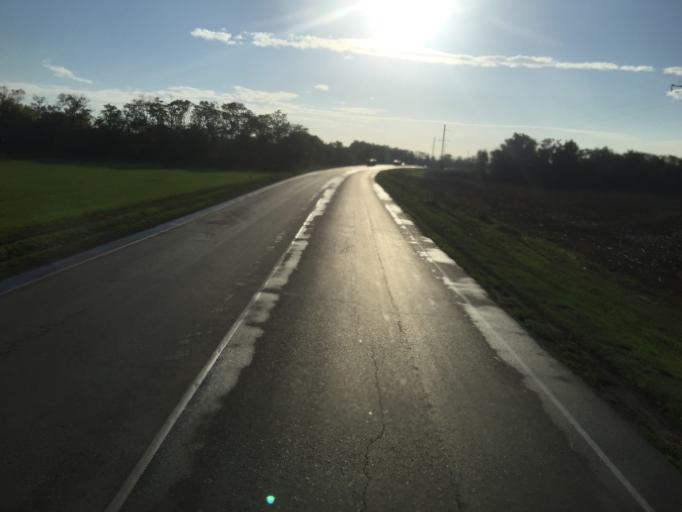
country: RU
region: Rostov
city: Mechetinskaya
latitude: 46.7892
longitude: 40.4016
